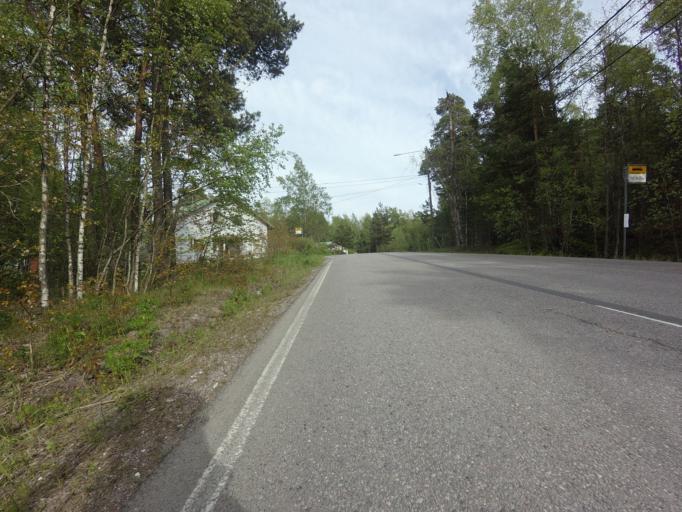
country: FI
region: Uusimaa
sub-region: Helsinki
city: Koukkuniemi
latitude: 60.1146
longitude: 24.7001
